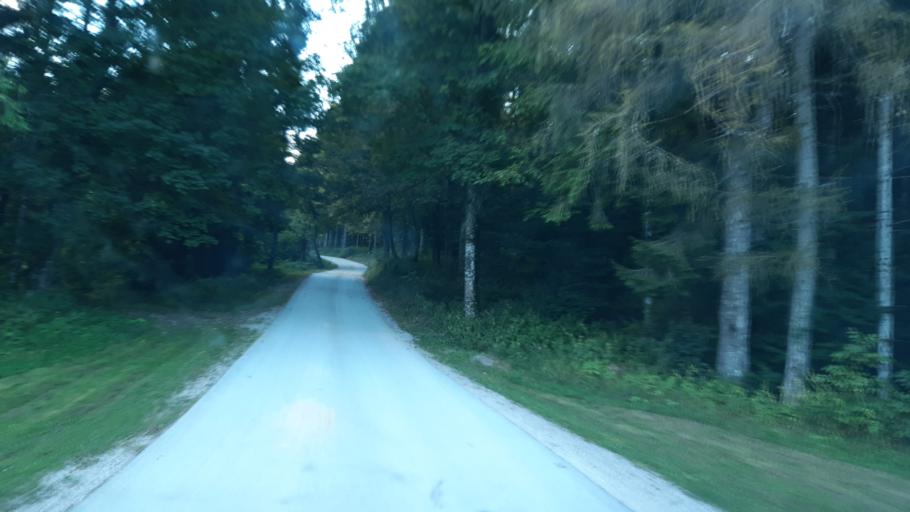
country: SI
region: Dolenjske Toplice
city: Dolenjske Toplice
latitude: 45.7144
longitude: 15.0117
